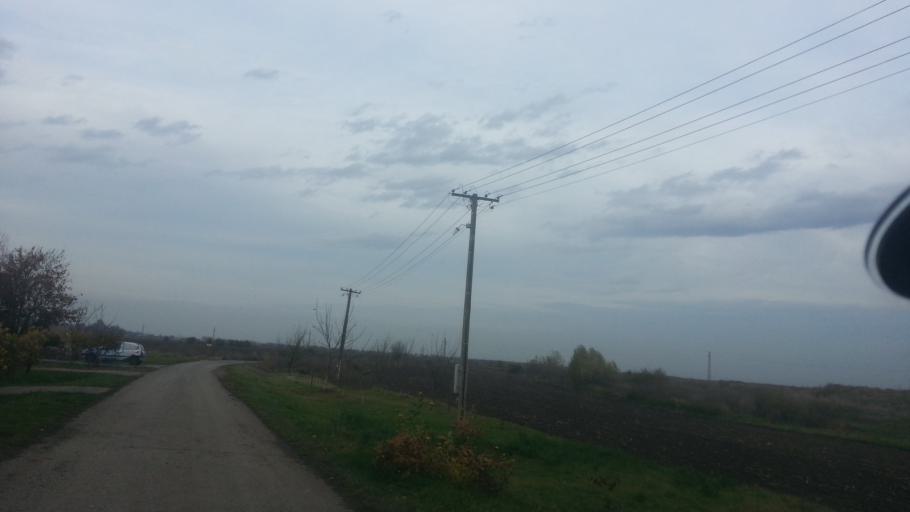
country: RS
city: Putinci
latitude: 44.9713
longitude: 19.9696
